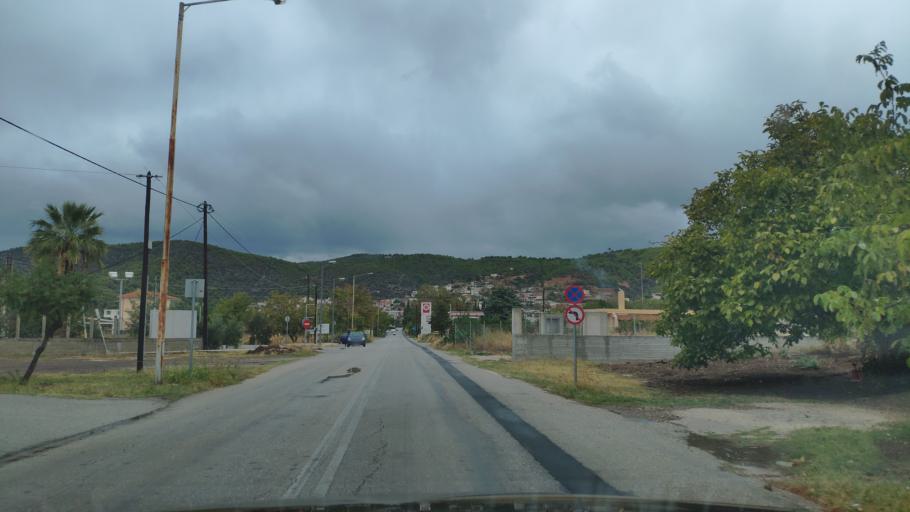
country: GR
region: Peloponnese
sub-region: Nomos Korinthias
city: Perachora
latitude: 38.0219
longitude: 22.9478
